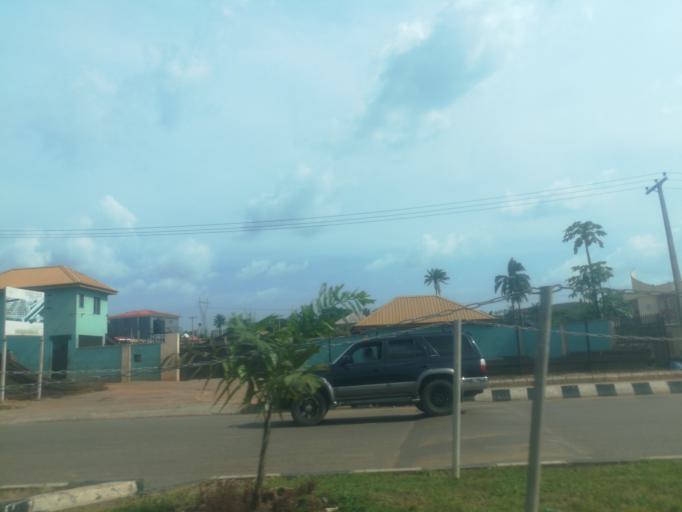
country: NG
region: Ogun
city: Abeokuta
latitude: 7.1292
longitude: 3.3598
